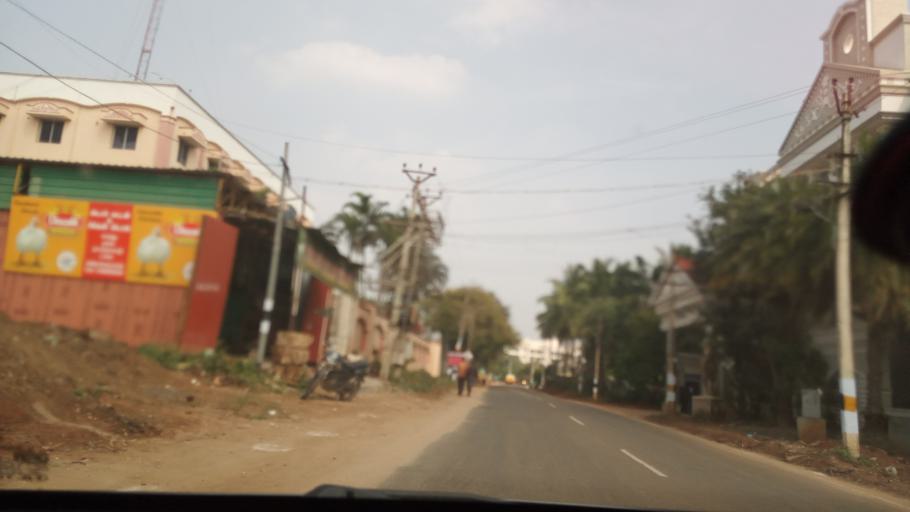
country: IN
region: Tamil Nadu
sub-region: Coimbatore
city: Perur
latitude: 11.0204
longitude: 76.8821
